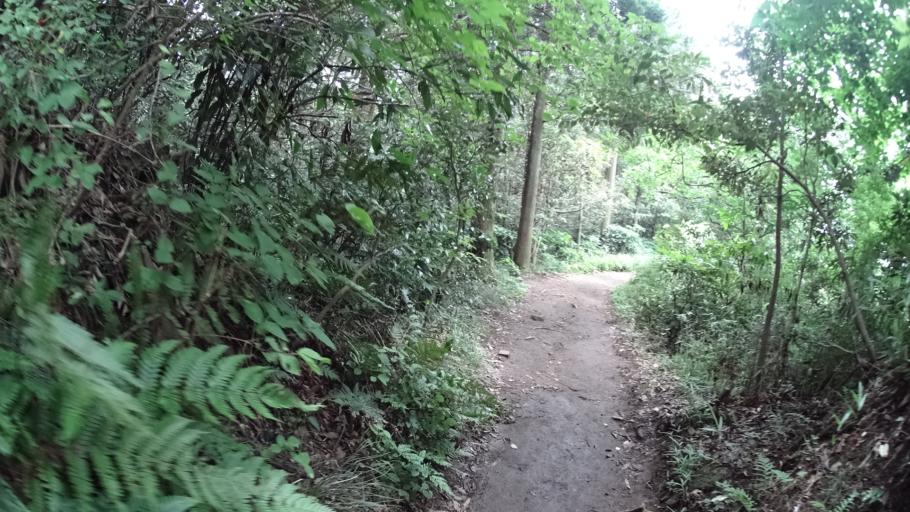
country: JP
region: Kanagawa
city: Zushi
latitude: 35.3374
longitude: 139.5881
